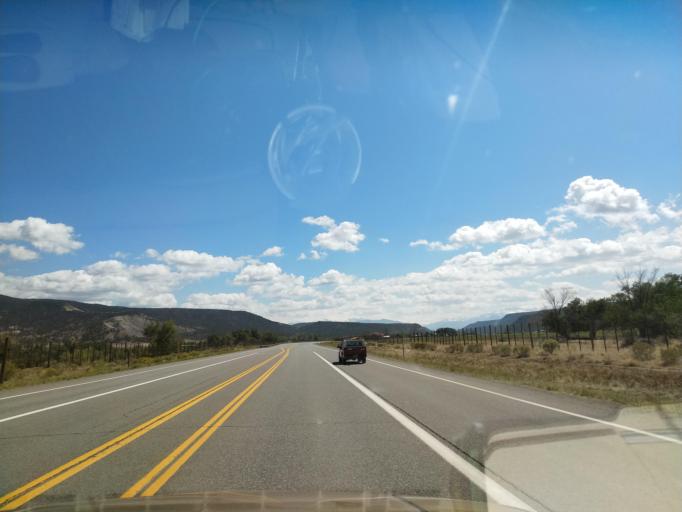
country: US
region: Colorado
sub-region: Montrose County
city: Montrose
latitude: 38.3256
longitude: -107.7786
